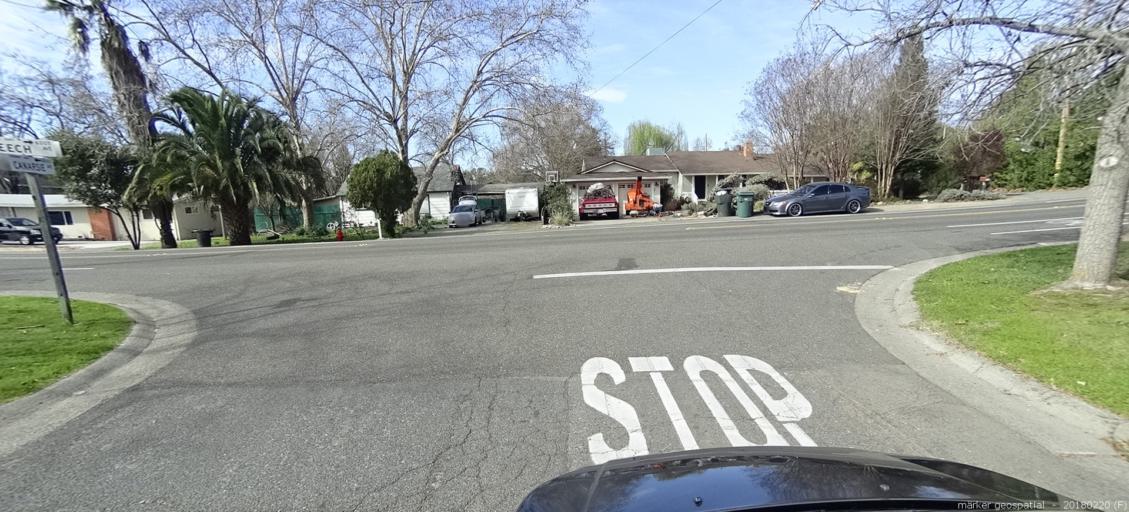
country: US
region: California
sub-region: Sacramento County
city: Orangevale
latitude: 38.6754
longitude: -121.2302
